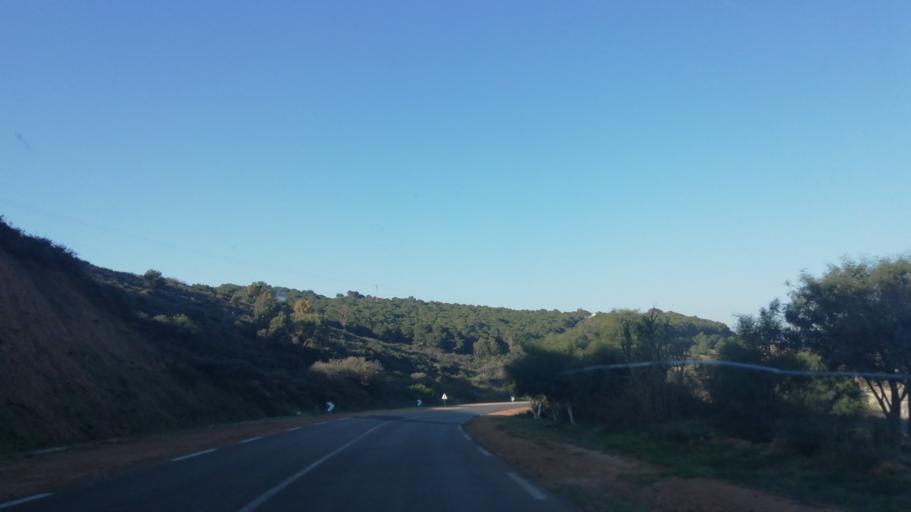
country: MA
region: Oriental
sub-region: Berkane-Taourirt
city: Ahfir
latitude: 35.0488
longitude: -2.1984
